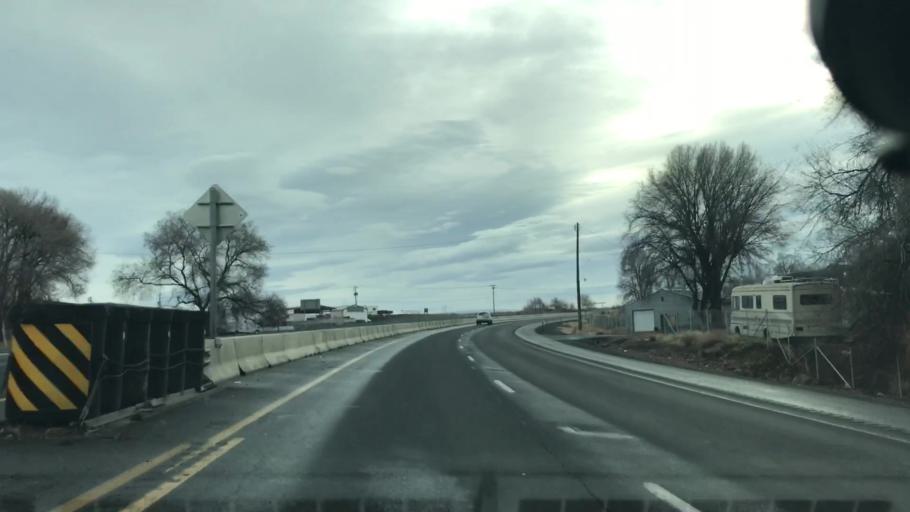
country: US
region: Washington
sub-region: Grant County
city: Moses Lake
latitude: 47.1387
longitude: -119.2598
